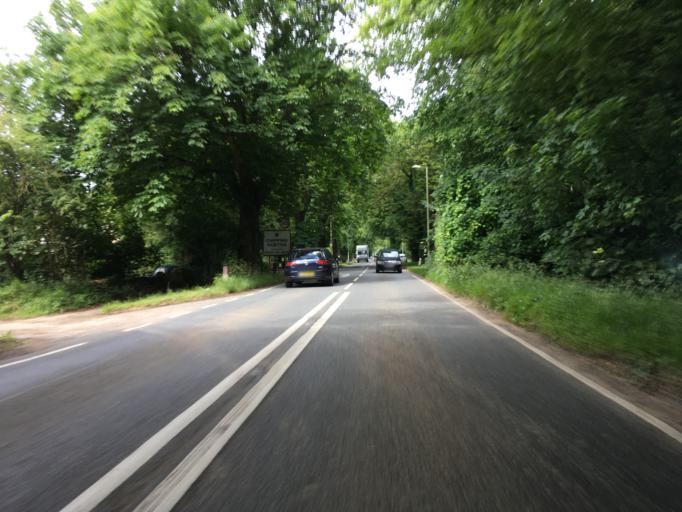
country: GB
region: England
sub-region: Oxfordshire
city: Chipping Norton
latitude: 51.9444
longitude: -1.5324
